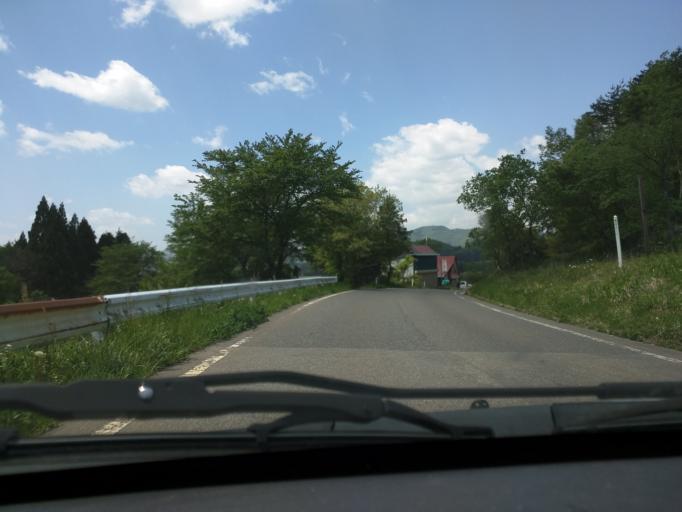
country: JP
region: Fukushima
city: Kitakata
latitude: 37.6388
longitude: 139.8006
